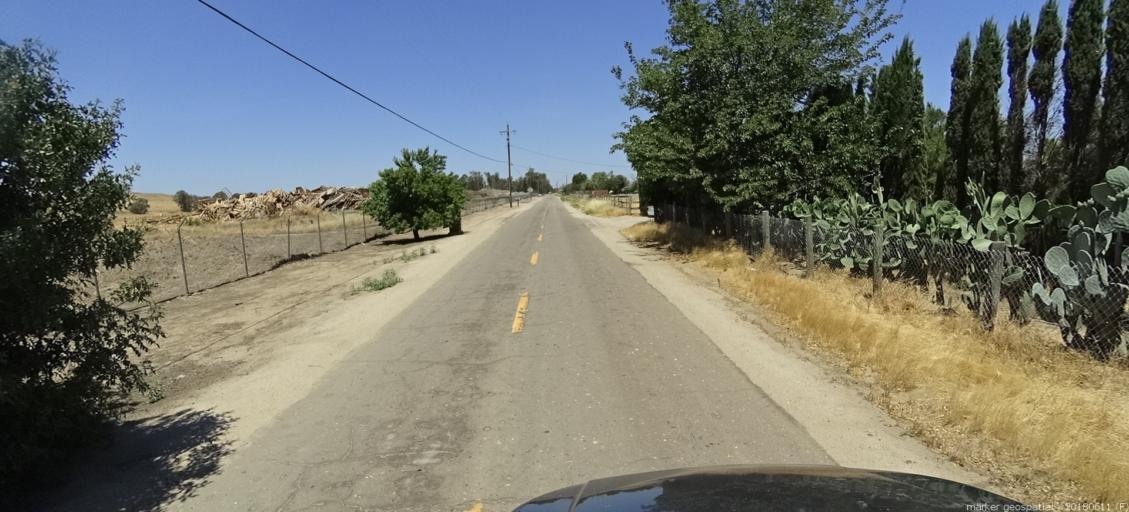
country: US
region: California
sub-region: Madera County
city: Fairmead
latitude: 37.0629
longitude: -120.1934
